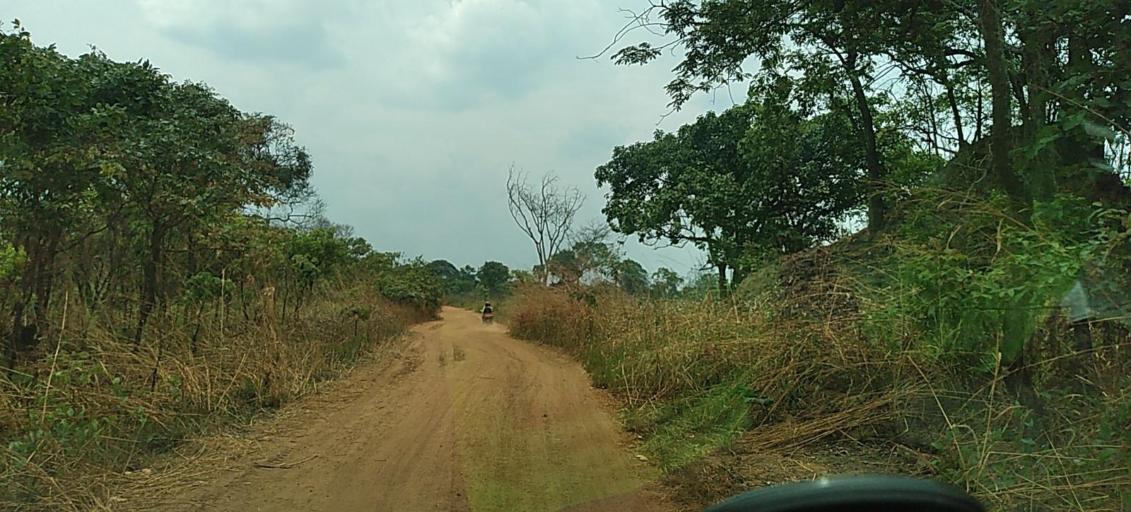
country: ZM
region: North-Western
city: Kansanshi
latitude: -12.0692
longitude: 26.3537
